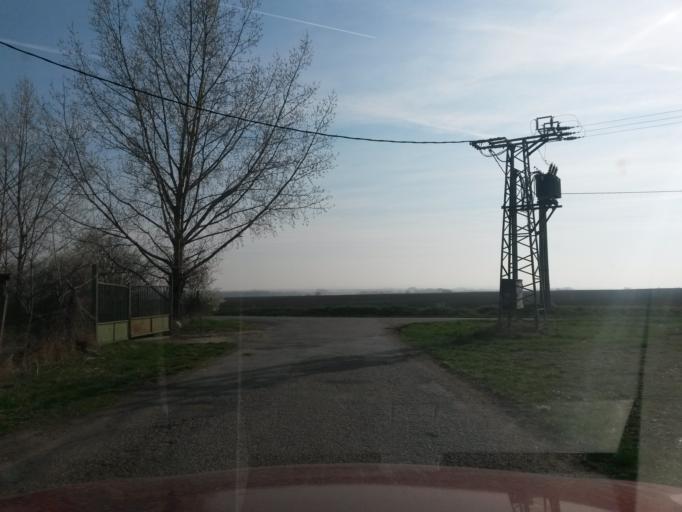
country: SK
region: Nitriansky
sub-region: Okres Komarno
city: Hurbanovo
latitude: 47.9163
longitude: 18.3049
